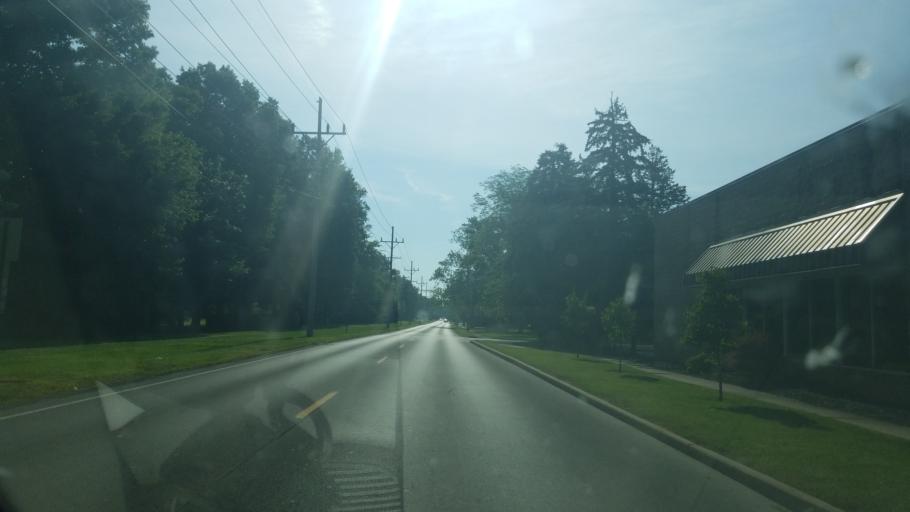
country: US
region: Ohio
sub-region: Hancock County
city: Findlay
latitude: 41.0224
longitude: -83.6486
